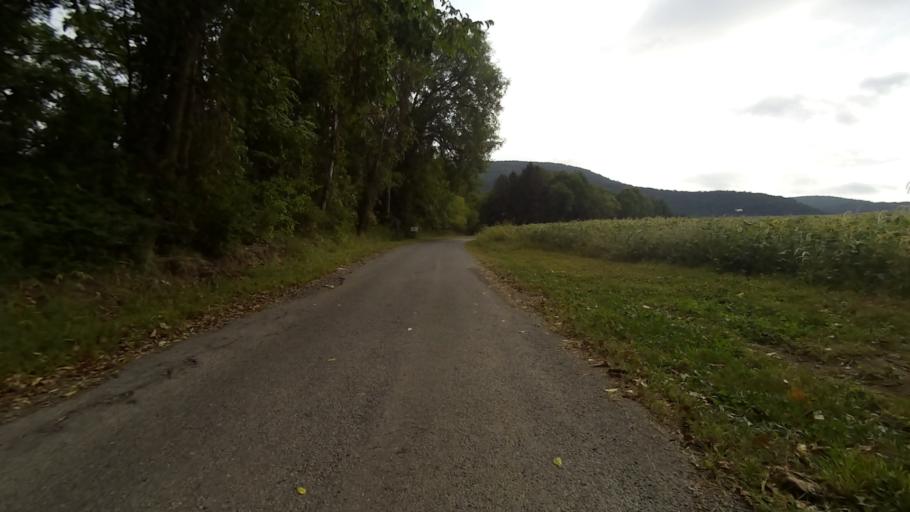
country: US
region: Pennsylvania
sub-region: Blair County
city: Williamsburg
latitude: 40.4944
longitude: -78.1764
